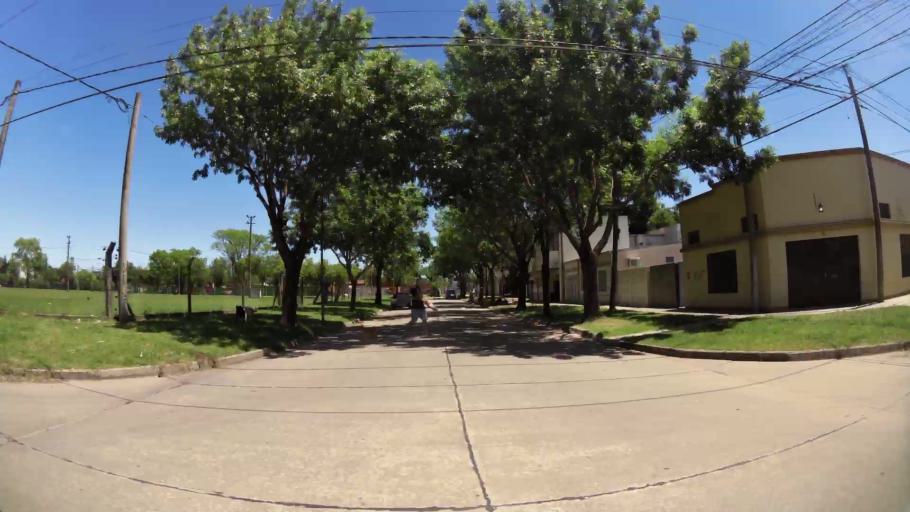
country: AR
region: Santa Fe
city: Rafaela
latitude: -31.2534
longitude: -61.4593
